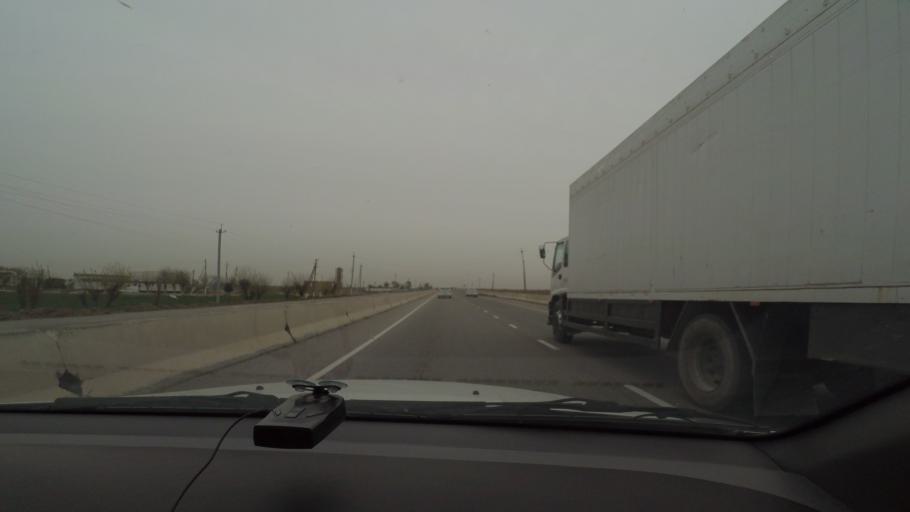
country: UZ
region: Jizzax
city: Gagarin
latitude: 40.4563
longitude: 68.2560
